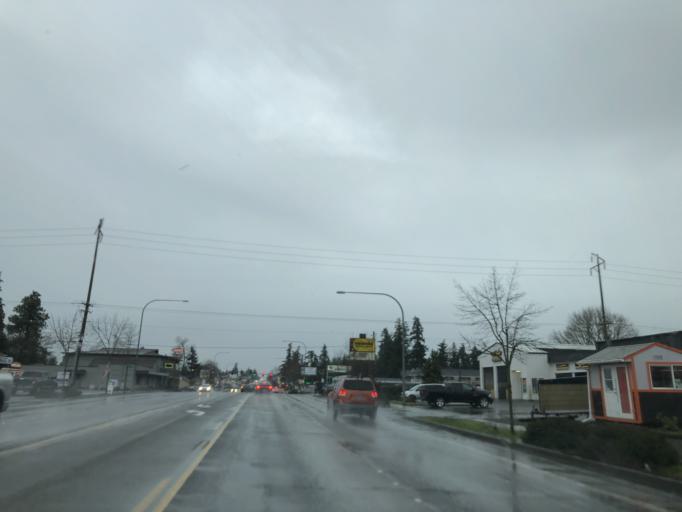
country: US
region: Washington
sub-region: Pierce County
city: Parkland
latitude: 47.1377
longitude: -122.4347
